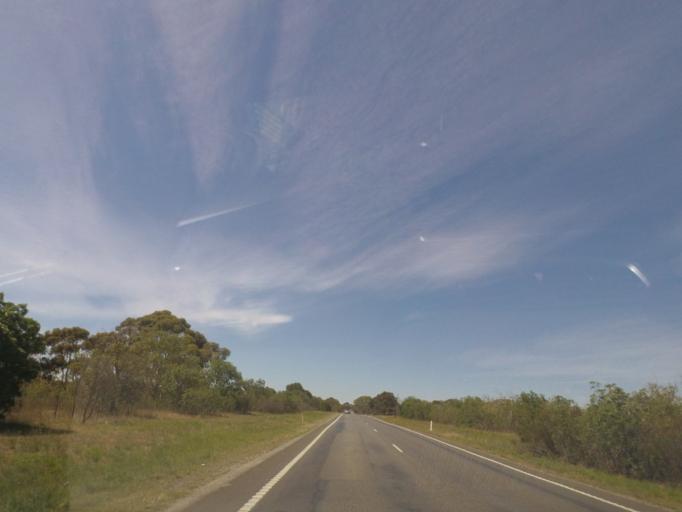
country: AU
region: Victoria
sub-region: Wyndham
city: Wyndham Vale
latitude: -37.8523
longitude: 144.3874
